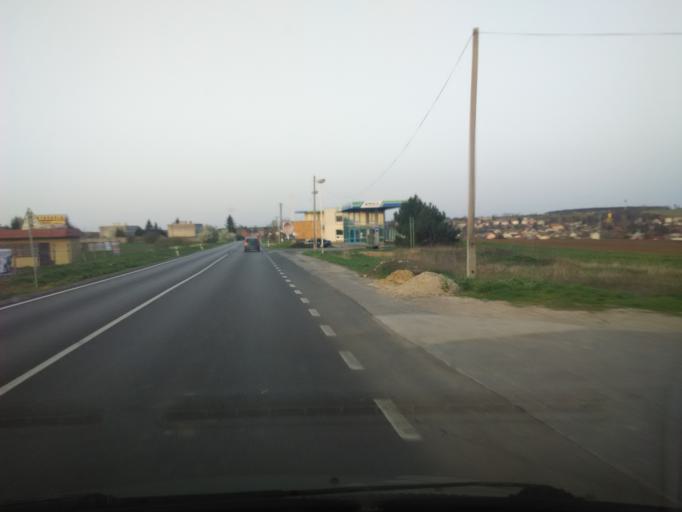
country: SK
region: Nitriansky
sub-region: Okres Nitra
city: Nitra
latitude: 48.2522
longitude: 18.0296
